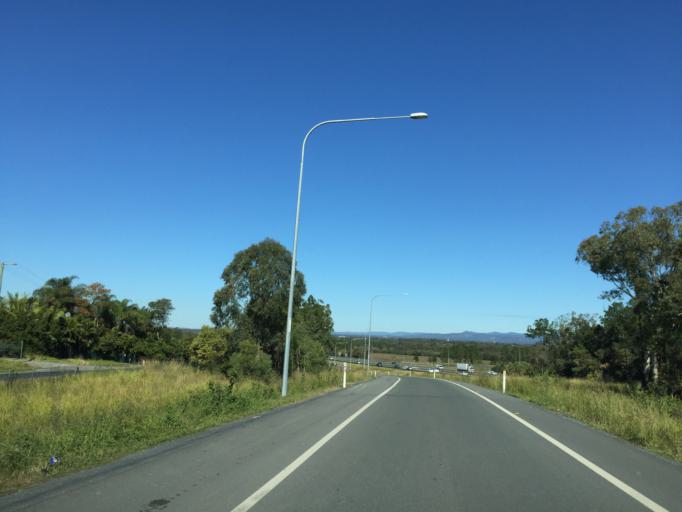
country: AU
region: Queensland
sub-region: Moreton Bay
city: Caboolture
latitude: -27.0404
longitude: 152.9791
